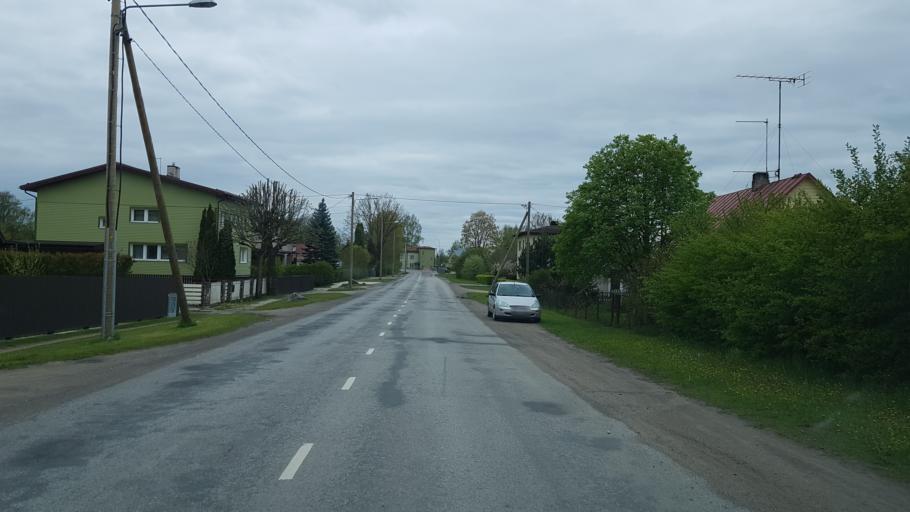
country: EE
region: Viljandimaa
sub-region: Viljandi linn
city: Viljandi
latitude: 58.3757
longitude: 25.6009
